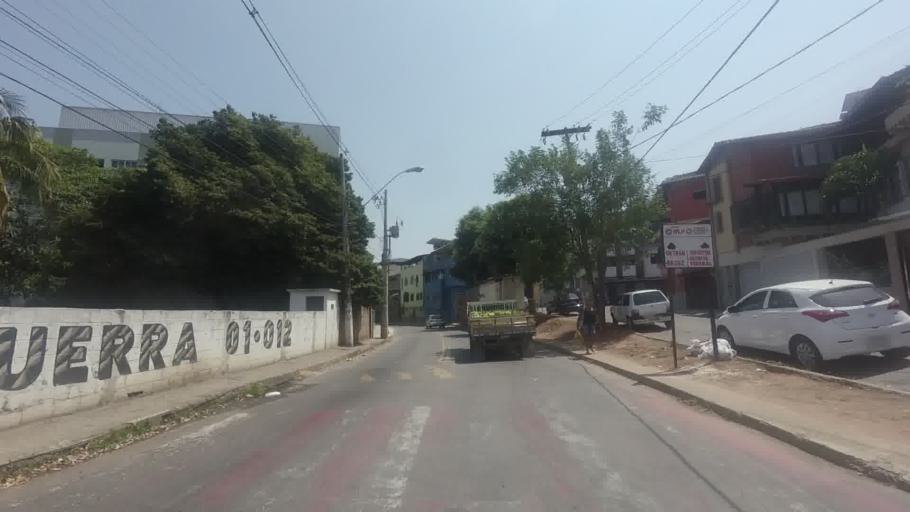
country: BR
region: Espirito Santo
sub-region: Cachoeiro De Itapemirim
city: Cachoeiro de Itapemirim
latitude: -20.8467
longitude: -41.1113
